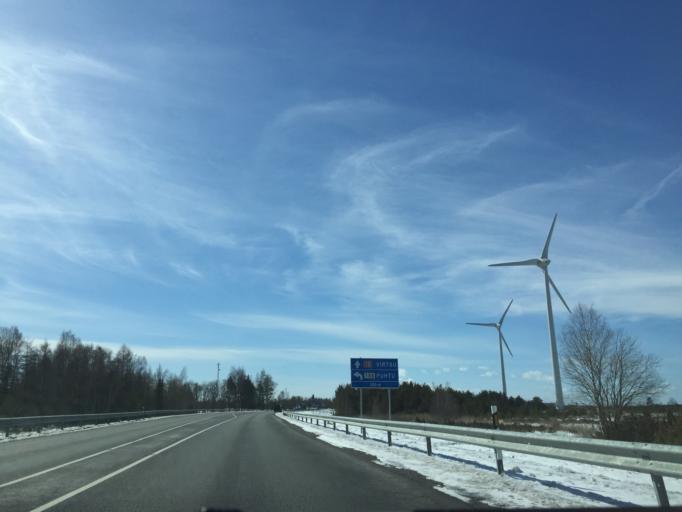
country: EE
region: Laeaene
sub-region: Lihula vald
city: Lihula
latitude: 58.5918
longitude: 23.5400
